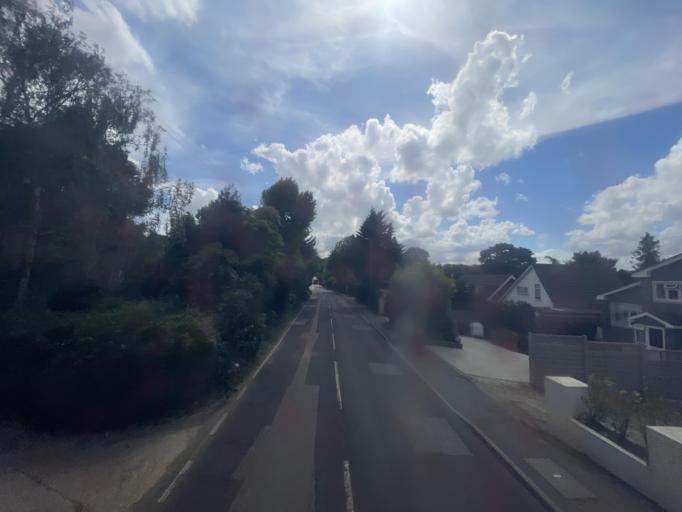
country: GB
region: England
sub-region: Kent
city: Biggin Hill
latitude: 51.3448
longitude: 0.0339
